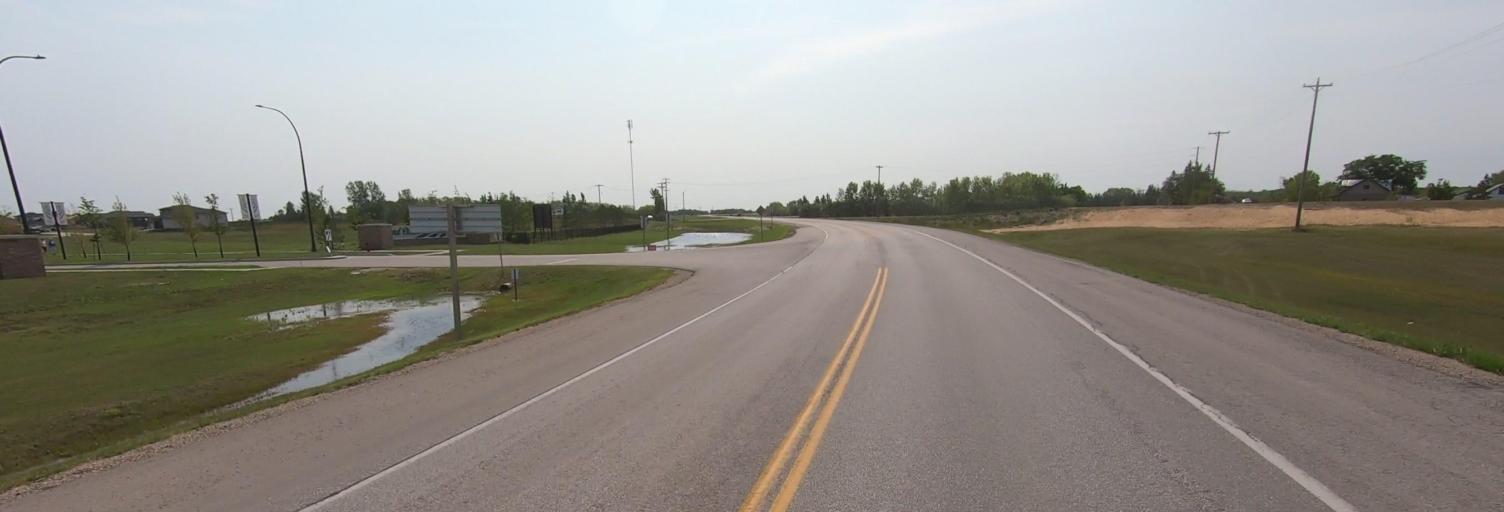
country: CA
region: Manitoba
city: Niverville
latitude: 49.6662
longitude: -97.1108
